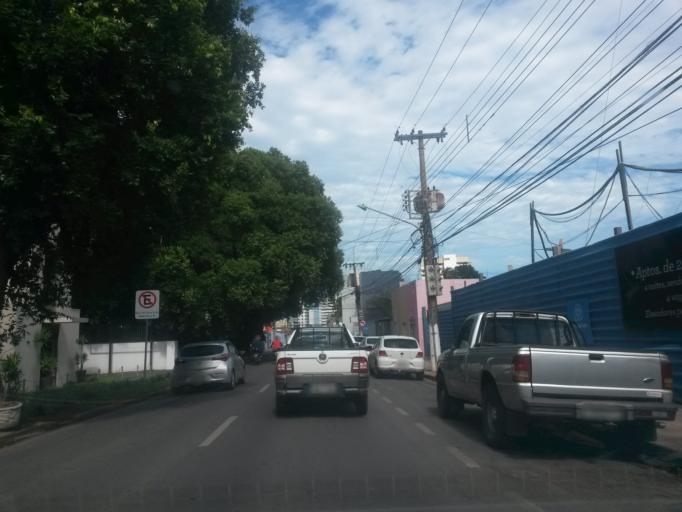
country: BR
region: Mato Grosso
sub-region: Cuiaba
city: Cuiaba
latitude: -15.5917
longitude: -56.1004
